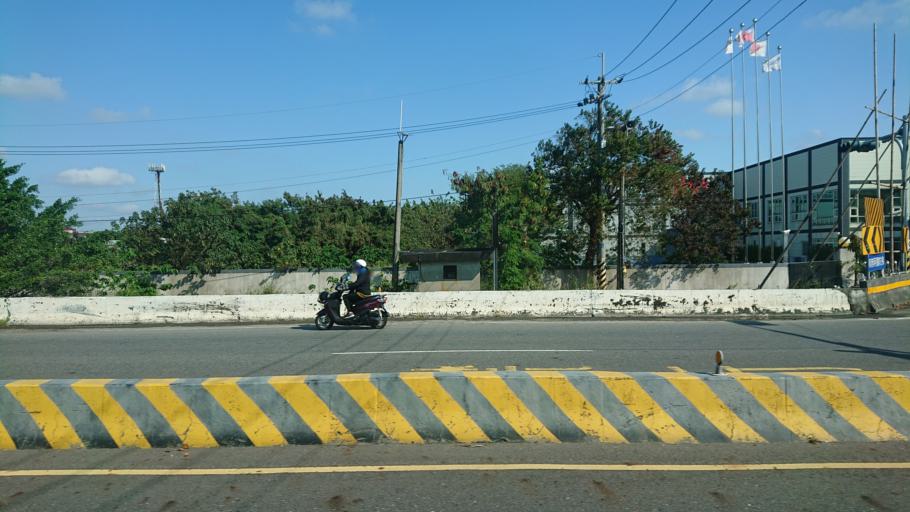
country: TW
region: Taiwan
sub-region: Chiayi
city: Taibao
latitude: 23.4435
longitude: 120.3710
